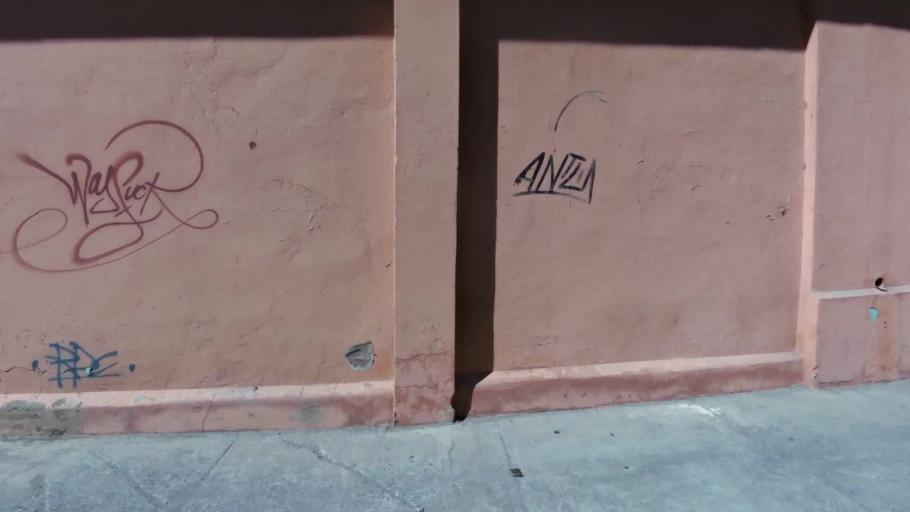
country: CL
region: O'Higgins
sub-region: Provincia de Cachapoal
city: Rancagua
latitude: -34.1757
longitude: -70.7452
